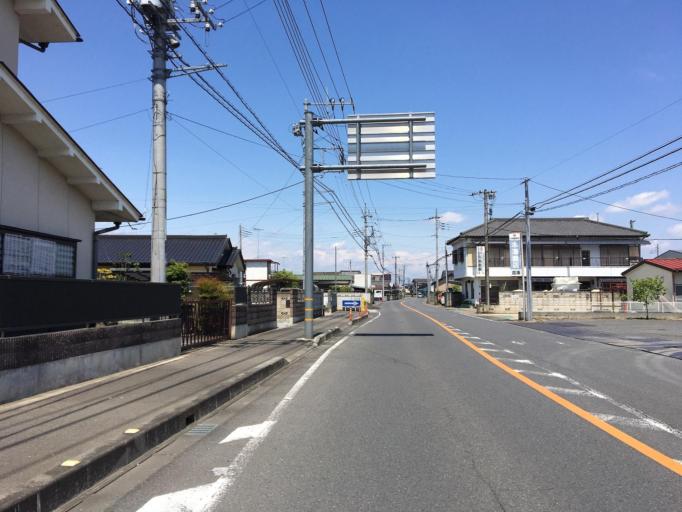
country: JP
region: Tochigi
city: Tochigi
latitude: 36.3630
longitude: 139.7224
